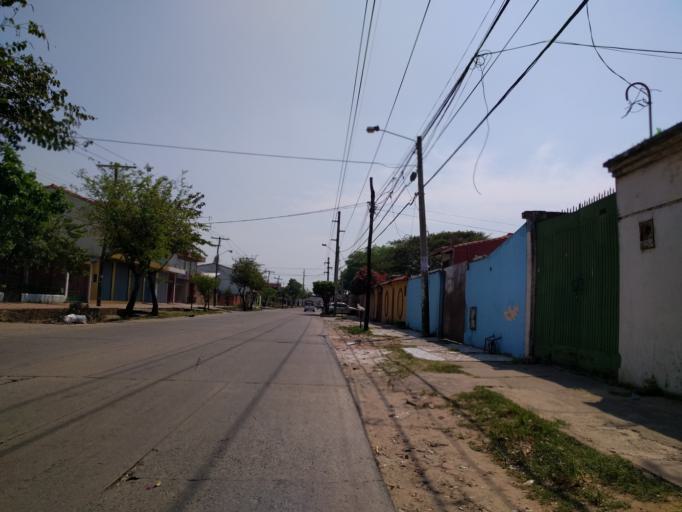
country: BO
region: Santa Cruz
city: Santa Cruz de la Sierra
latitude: -17.7944
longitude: -63.1566
